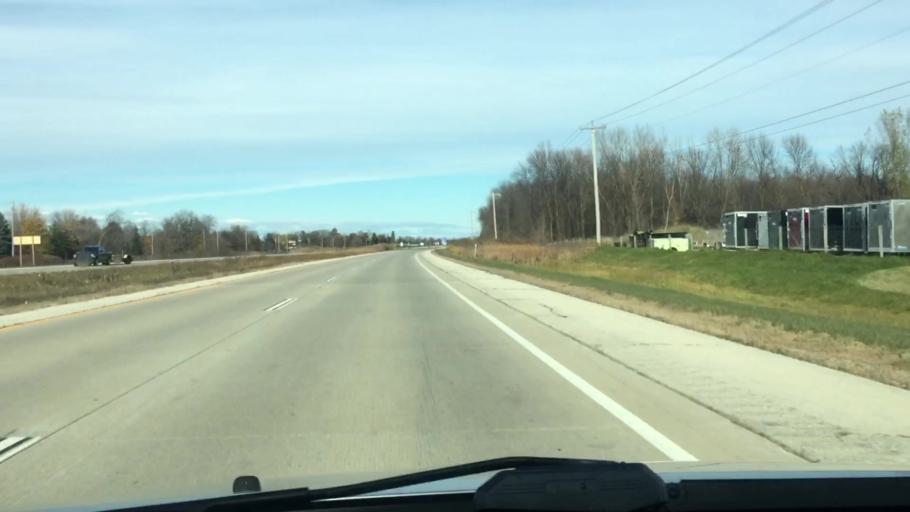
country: US
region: Wisconsin
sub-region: Brown County
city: Bellevue
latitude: 44.5689
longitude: -87.8779
